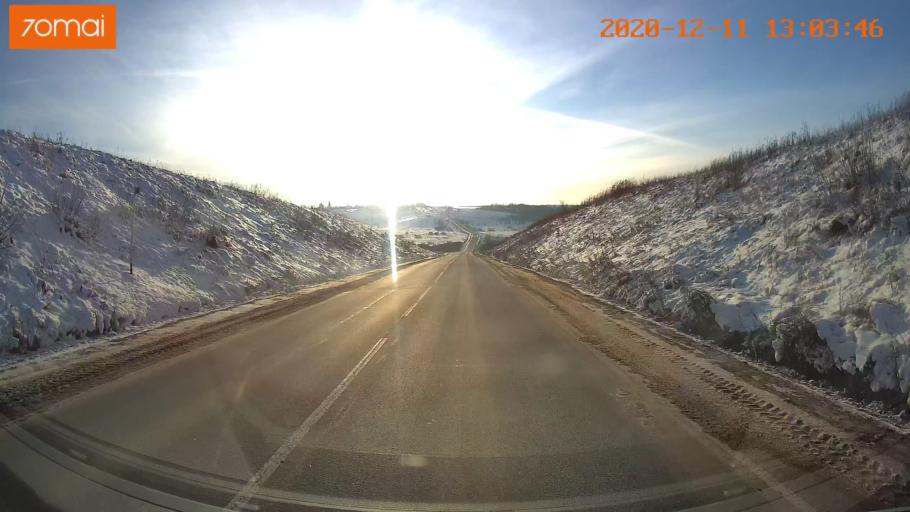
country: RU
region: Kostroma
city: Chistyye Bory
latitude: 58.2657
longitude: 41.6723
